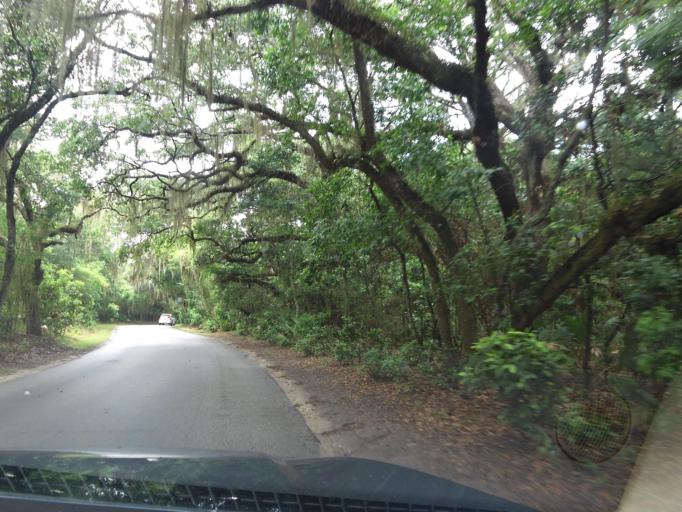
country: US
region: Florida
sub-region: Nassau County
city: Fernandina Beach
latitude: 30.7009
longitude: -81.4457
